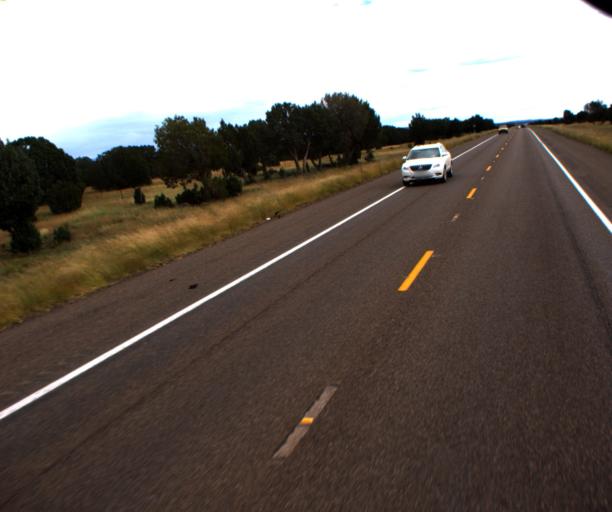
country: US
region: Arizona
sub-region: Navajo County
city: Show Low
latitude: 34.2971
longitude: -110.0337
